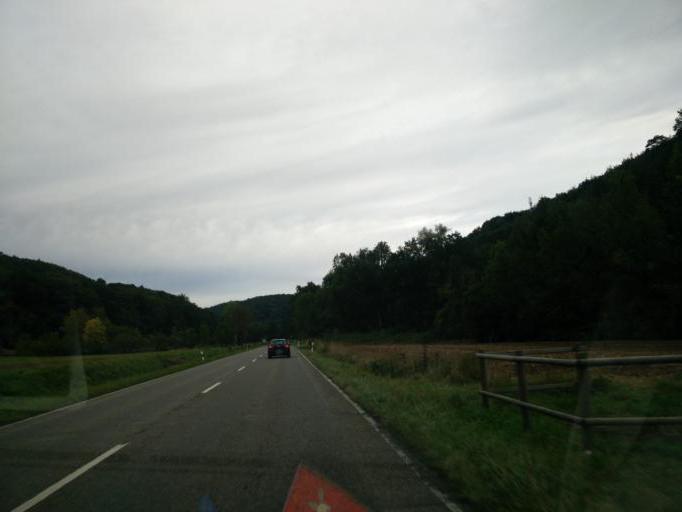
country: DE
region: Baden-Wuerttemberg
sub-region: Tuebingen Region
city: Tuebingen
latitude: 48.5395
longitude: 9.0766
